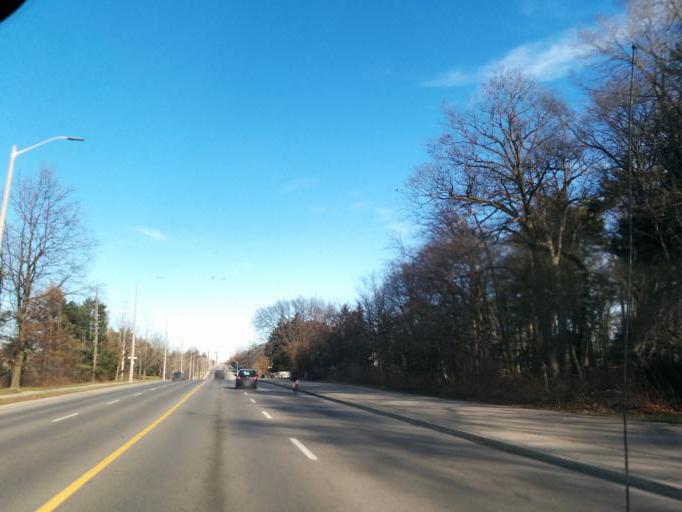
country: CA
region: Ontario
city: Mississauga
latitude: 43.5343
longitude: -79.6045
